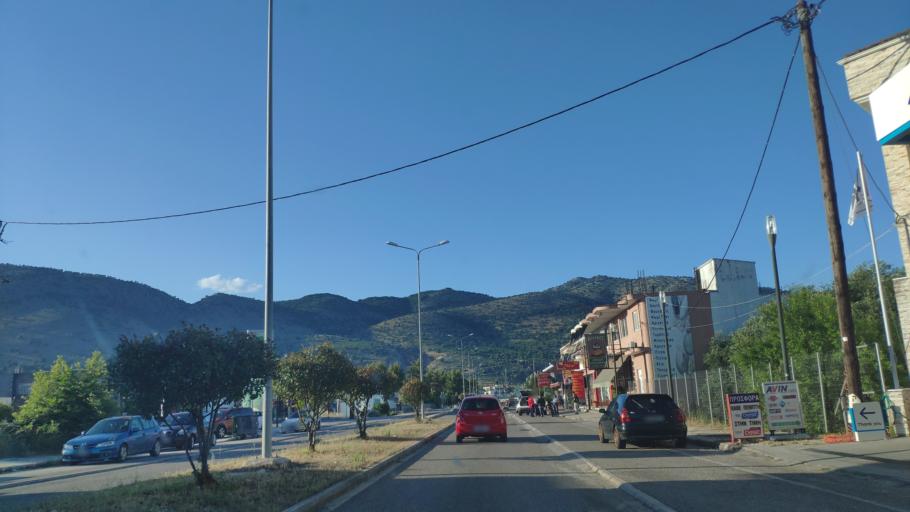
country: GR
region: Epirus
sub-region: Nomos Prevezis
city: Louros
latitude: 39.1614
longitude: 20.7541
